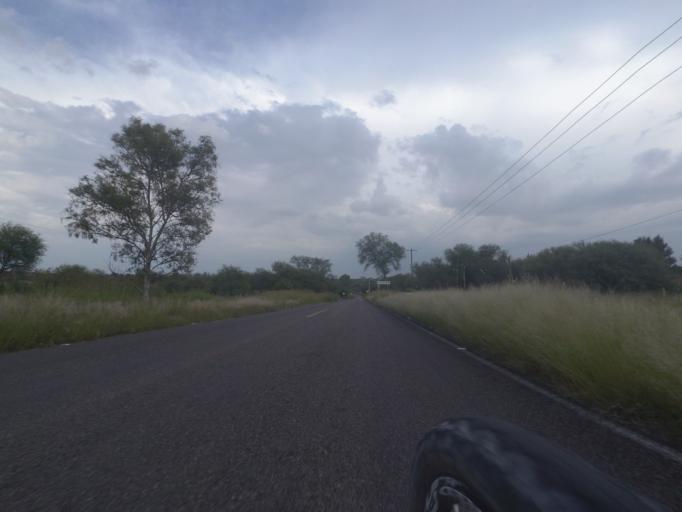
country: MX
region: Aguascalientes
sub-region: Aguascalientes
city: La Loma de los Negritos
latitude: 21.8360
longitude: -102.3710
